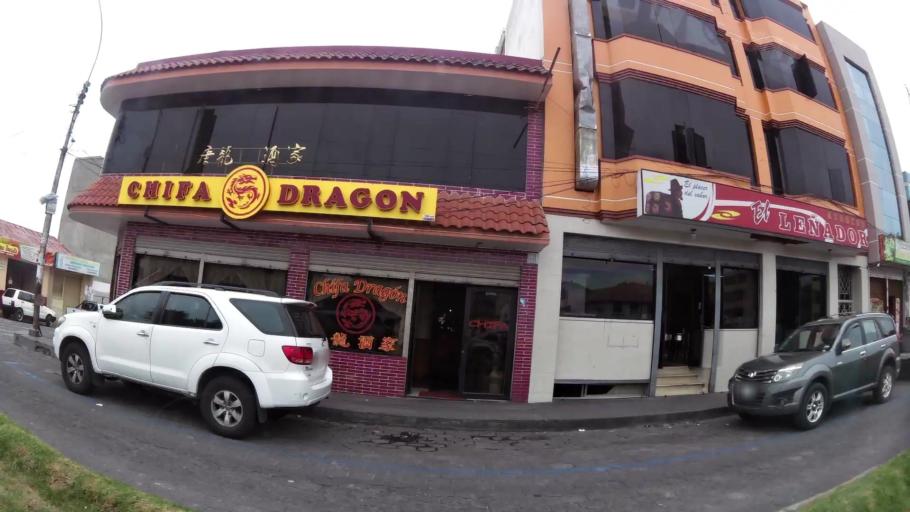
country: EC
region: Cotopaxi
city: Latacunga
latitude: -0.9338
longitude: -78.6179
